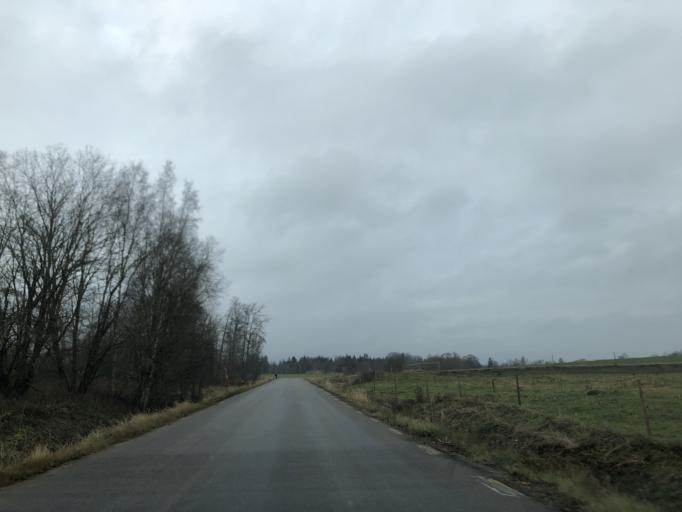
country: SE
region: Vaestra Goetaland
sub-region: Ulricehamns Kommun
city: Ulricehamn
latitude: 57.8836
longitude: 13.5140
